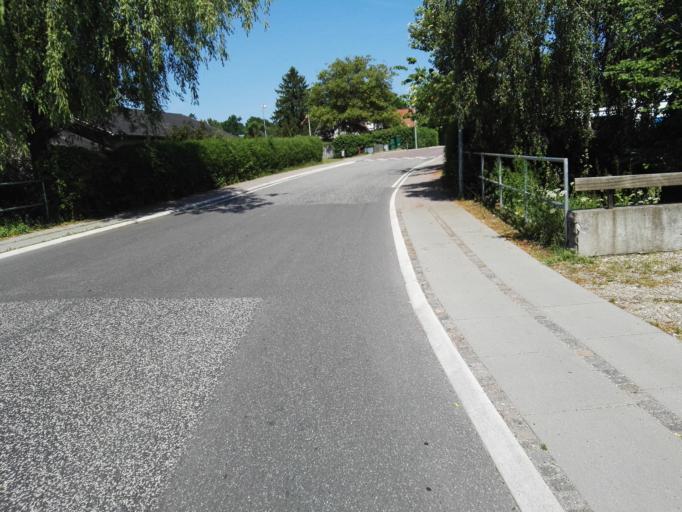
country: DK
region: Capital Region
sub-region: Fureso Kommune
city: Vaerlose
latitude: 55.7613
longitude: 12.3928
